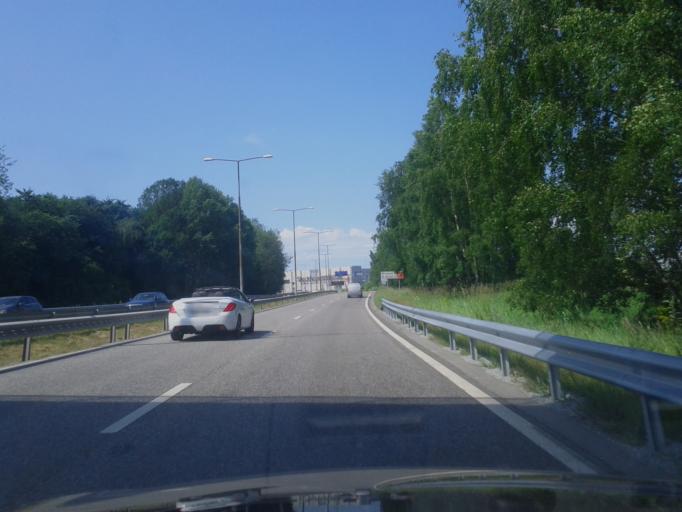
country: SE
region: Stockholm
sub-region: Stockholms Kommun
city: Arsta
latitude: 59.2779
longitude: 18.0265
